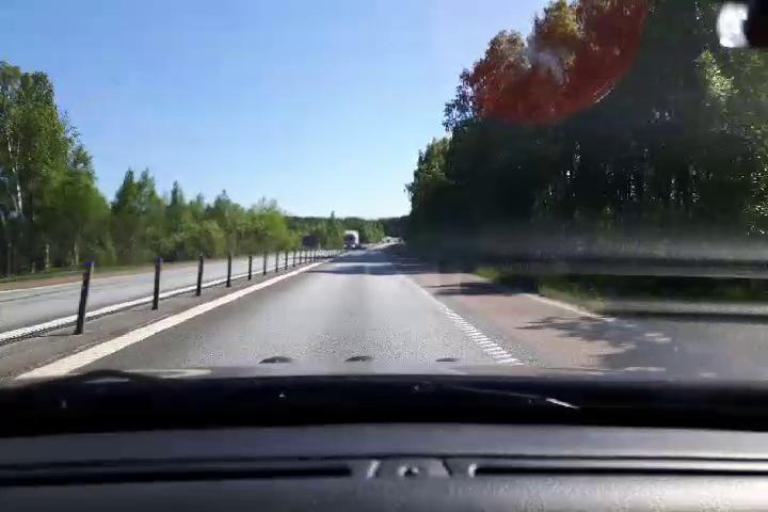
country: SE
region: Gaevleborg
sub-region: Soderhamns Kommun
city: Soderhamn
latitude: 61.2792
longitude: 17.0272
